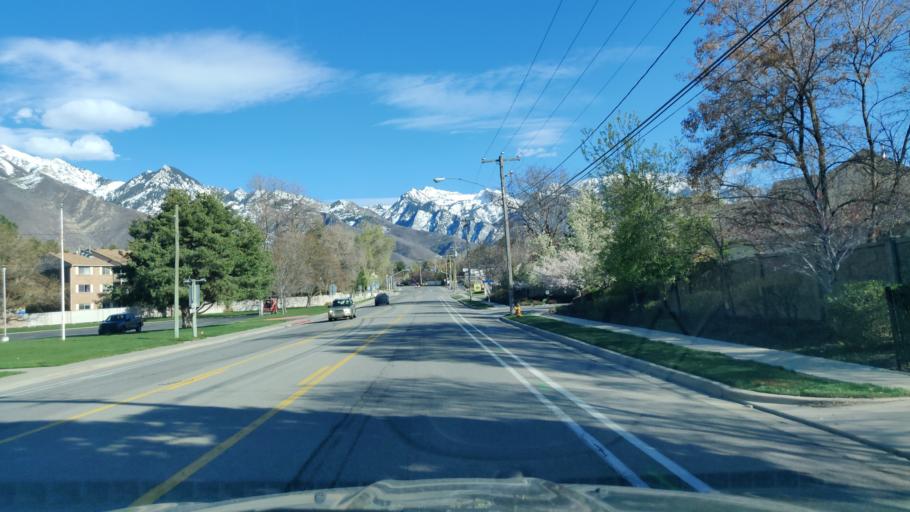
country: US
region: Utah
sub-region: Salt Lake County
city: Little Cottonwood Creek Valley
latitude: 40.6119
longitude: -111.8201
